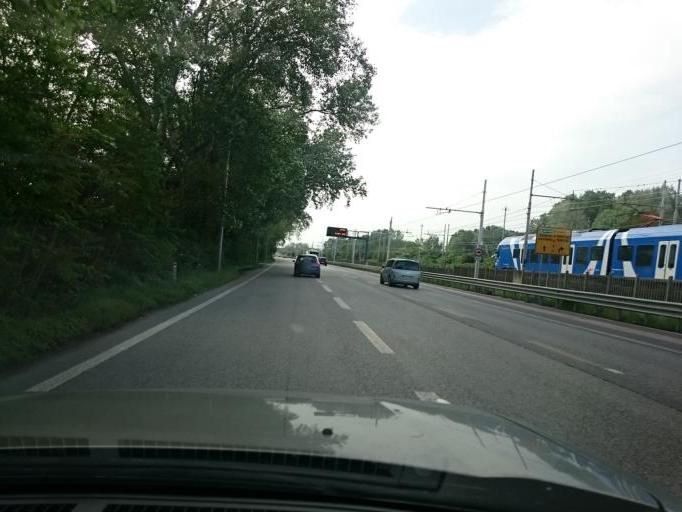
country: IT
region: Veneto
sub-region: Provincia di Venezia
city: Campalto
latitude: 45.4665
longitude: 12.2756
